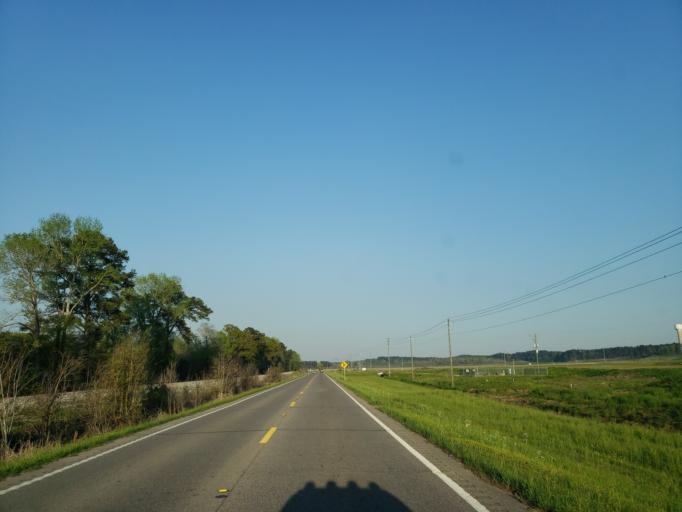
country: US
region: Mississippi
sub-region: Lauderdale County
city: Marion
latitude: 32.3941
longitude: -88.6345
